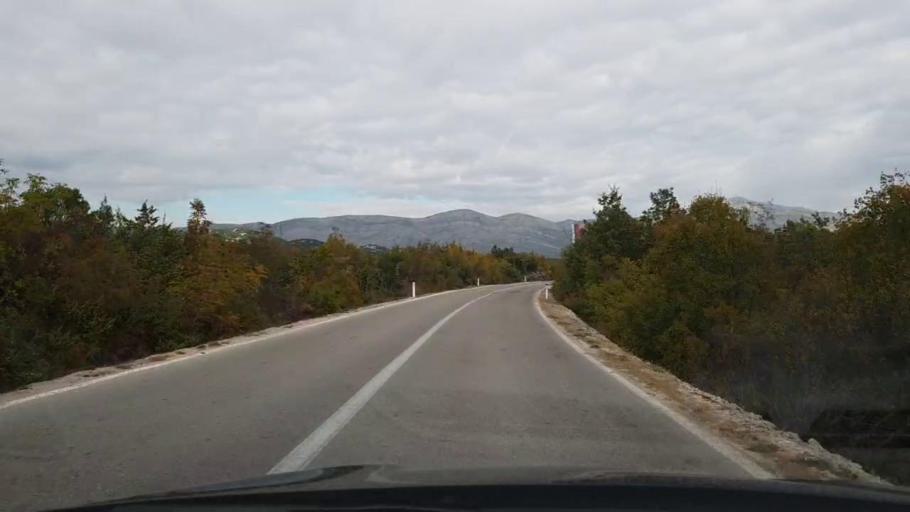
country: HR
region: Dubrovacko-Neretvanska
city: Cibaca
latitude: 42.6730
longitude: 18.2316
